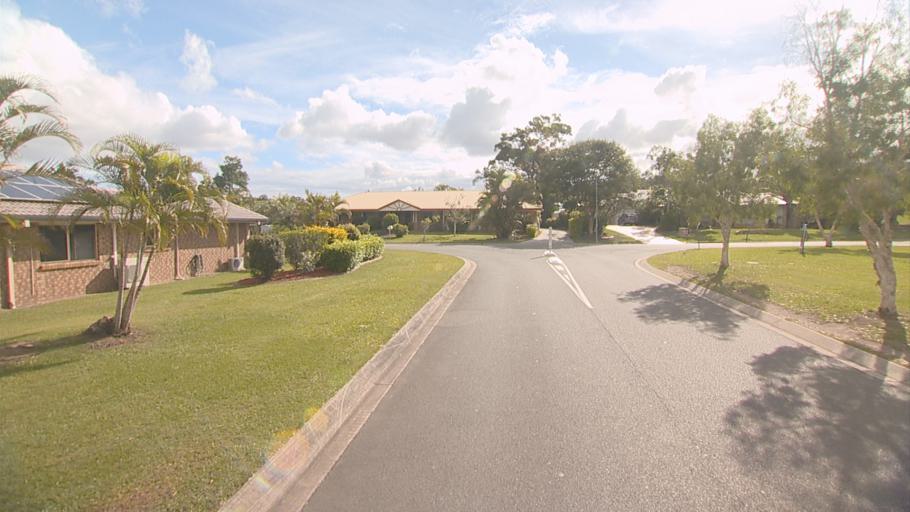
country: AU
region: Queensland
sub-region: Logan
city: Beenleigh
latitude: -27.6595
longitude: 153.2064
